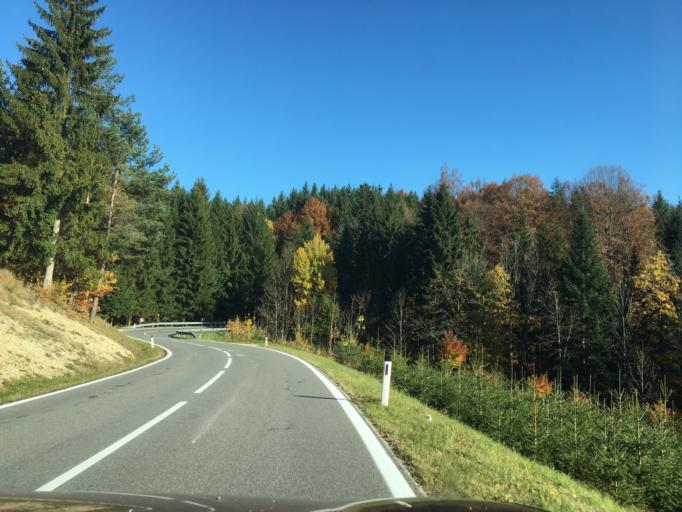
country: AT
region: Lower Austria
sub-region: Politischer Bezirk Zwettl
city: Langschlag
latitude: 48.4613
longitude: 14.7674
